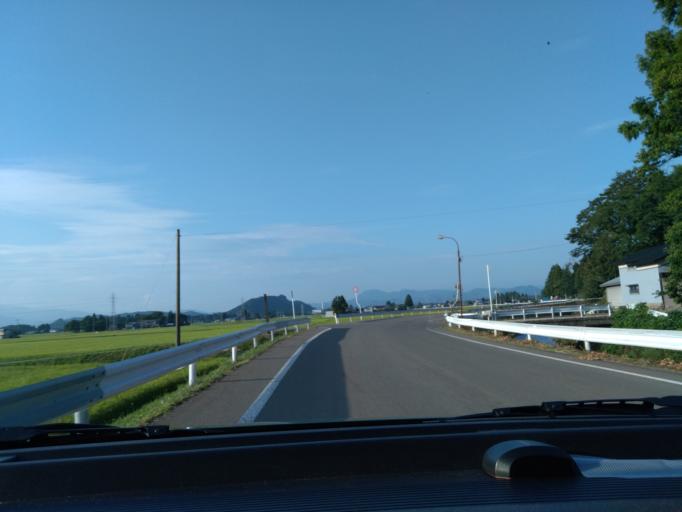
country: JP
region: Akita
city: Kakunodatemachi
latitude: 39.5606
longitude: 140.5745
